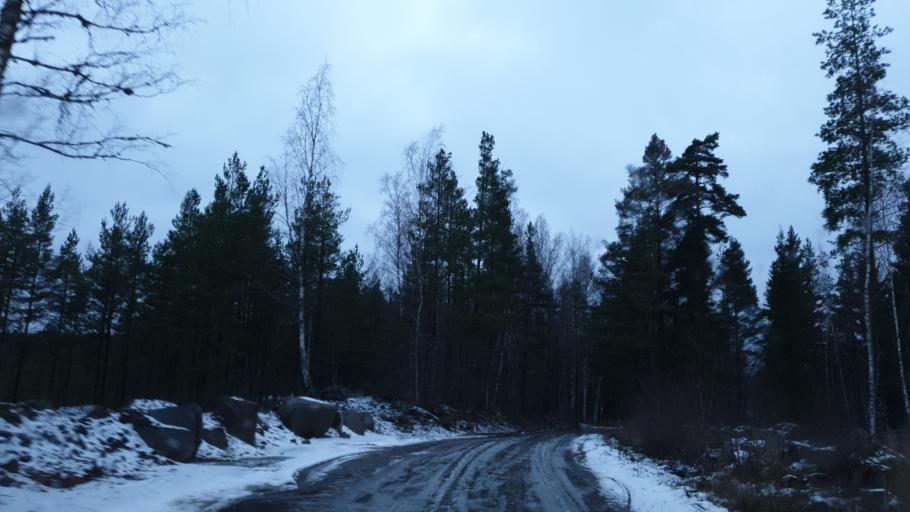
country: SE
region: Uppsala
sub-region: Tierps Kommun
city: Tierp
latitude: 60.3441
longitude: 17.4686
